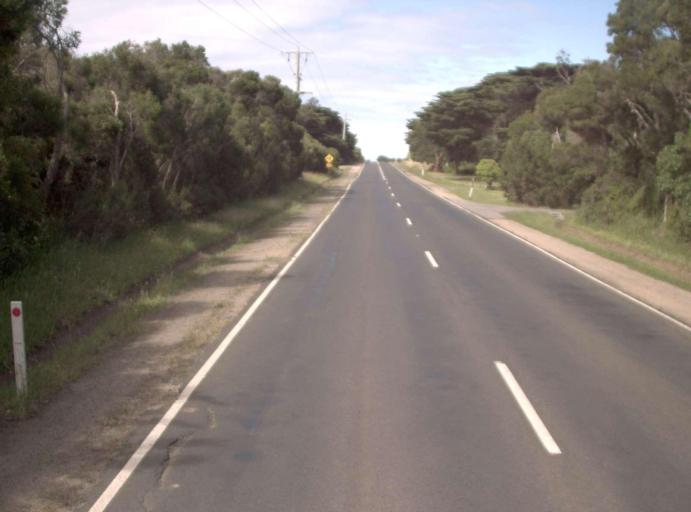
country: AU
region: Victoria
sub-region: Bass Coast
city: Phillip Island
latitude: -38.4812
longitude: 145.1773
